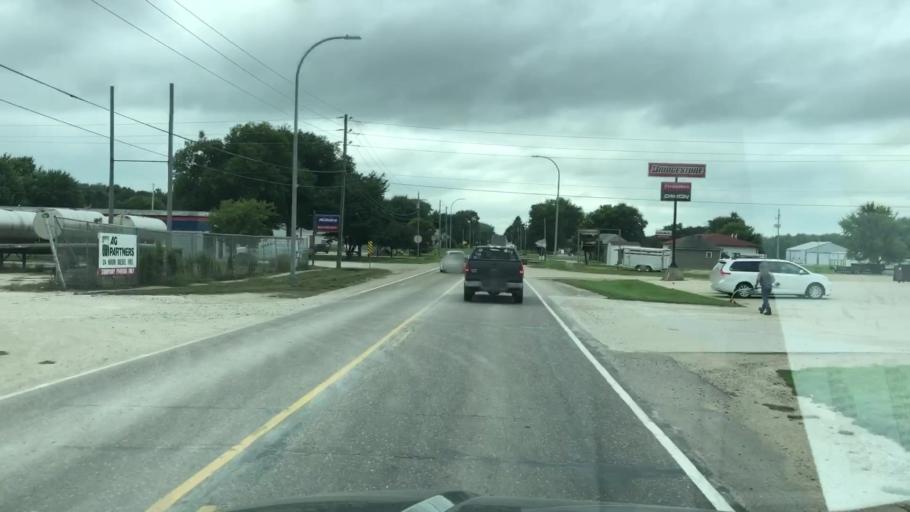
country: US
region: Iowa
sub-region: O'Brien County
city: Sheldon
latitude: 43.1859
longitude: -95.8563
